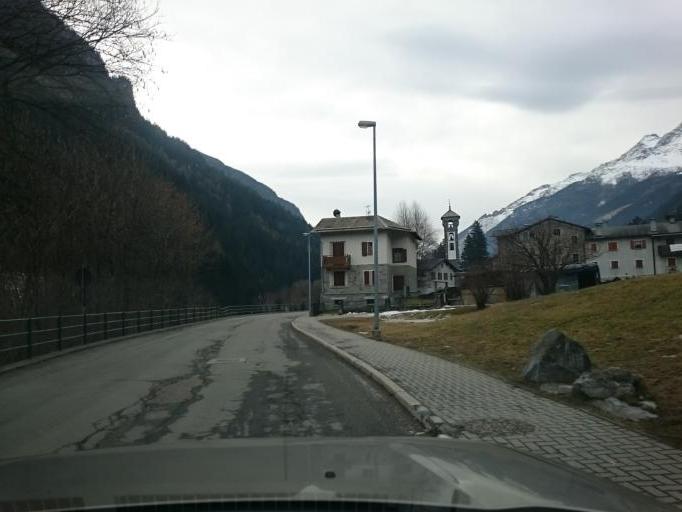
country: IT
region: Lombardy
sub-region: Provincia di Sondrio
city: Valdisotto
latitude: 46.4294
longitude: 10.3562
